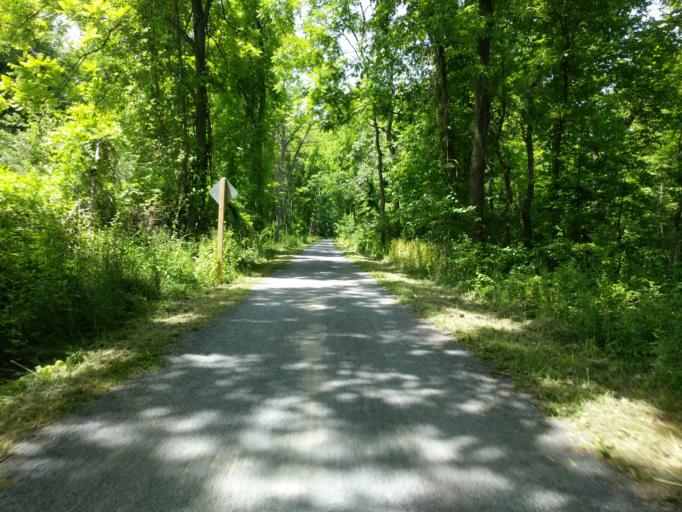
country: US
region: New York
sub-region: Tompkins County
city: Northwest Ithaca
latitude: 42.4736
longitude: -76.5320
